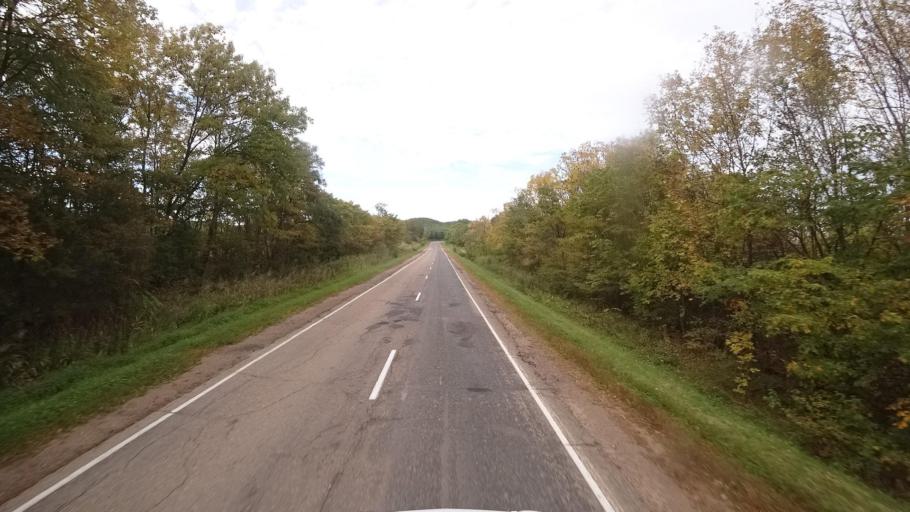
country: RU
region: Primorskiy
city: Dostoyevka
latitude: 44.3671
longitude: 133.4332
